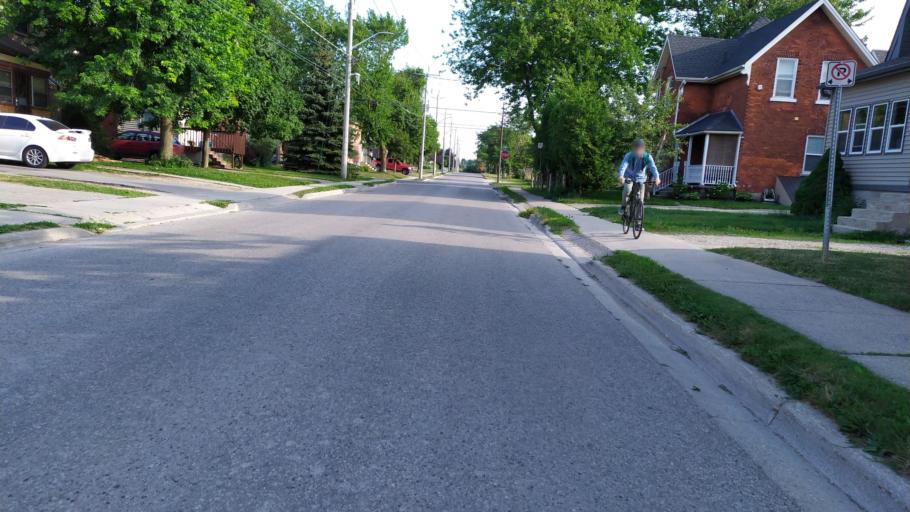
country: CA
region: Ontario
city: Stratford
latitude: 43.3677
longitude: -80.9667
